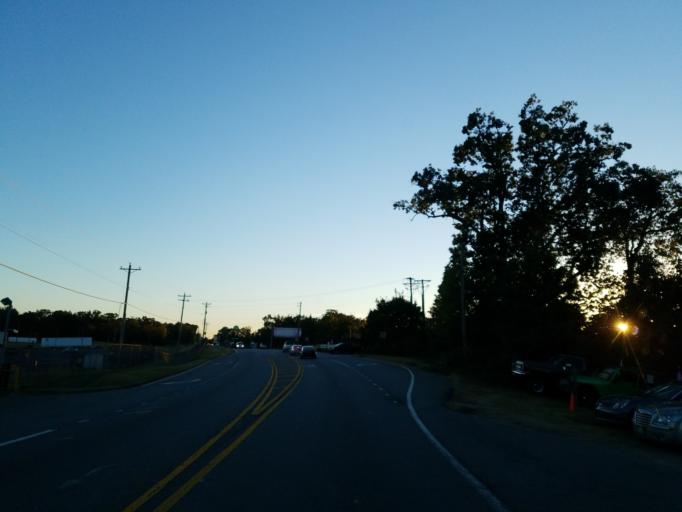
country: US
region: Georgia
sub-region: Forsyth County
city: Cumming
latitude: 34.1680
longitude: -84.1657
